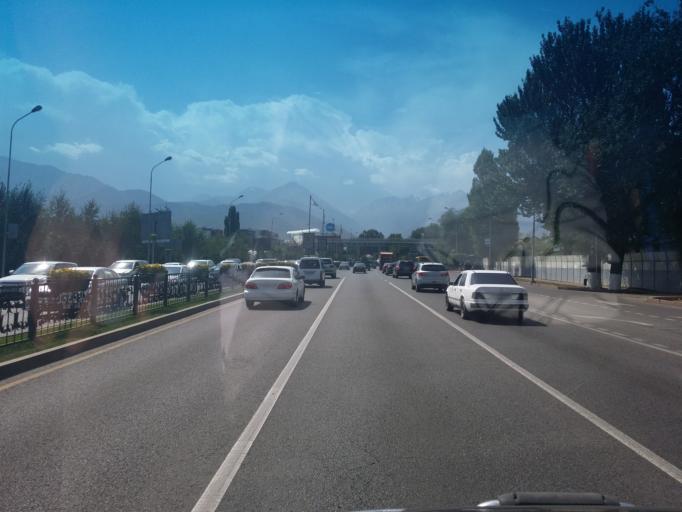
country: KZ
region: Almaty Qalasy
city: Almaty
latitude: 43.2061
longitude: 76.9136
